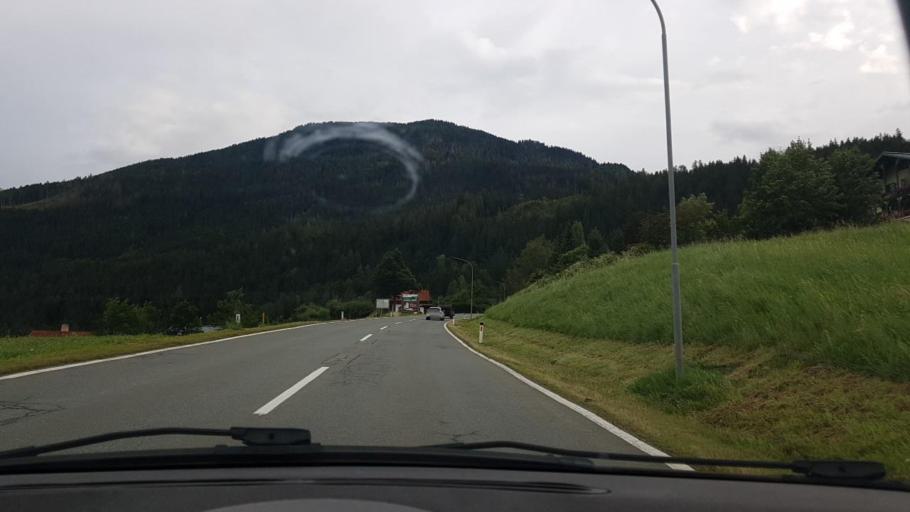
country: AT
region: Carinthia
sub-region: Politischer Bezirk Spittal an der Drau
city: Winklern
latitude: 46.8673
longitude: 12.8755
